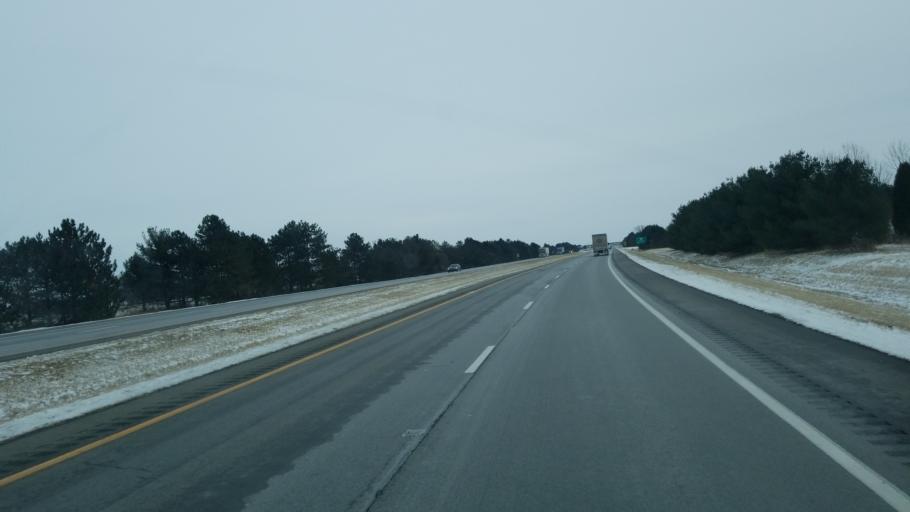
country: US
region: Ohio
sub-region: Wyandot County
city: Carey
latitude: 40.9790
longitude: -83.4950
